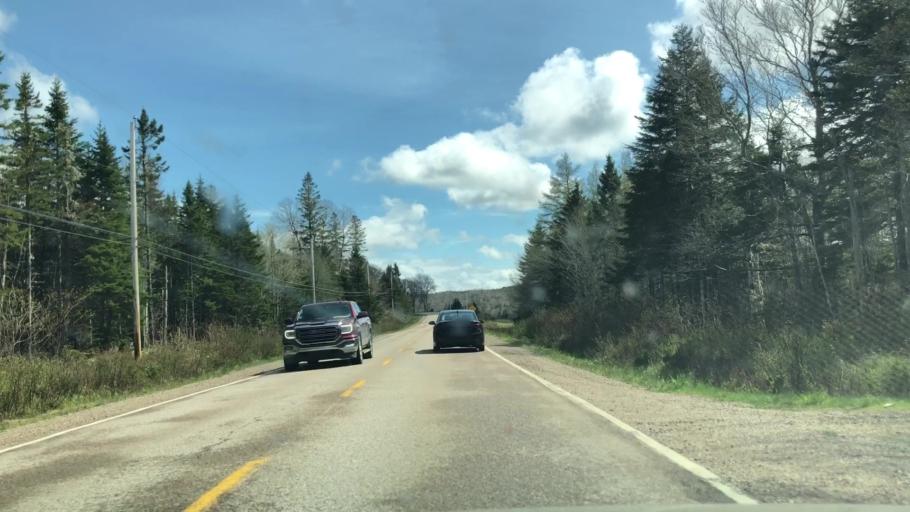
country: CA
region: Nova Scotia
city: Antigonish
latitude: 45.2045
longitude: -62.0037
